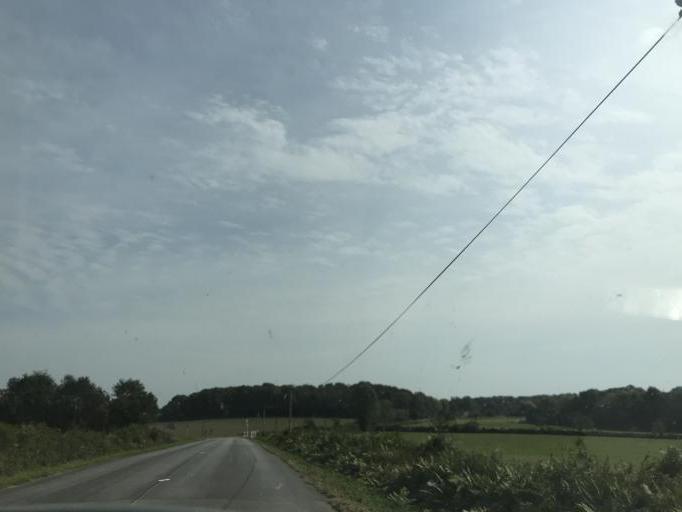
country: FR
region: Brittany
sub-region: Departement du Finistere
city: Loperec
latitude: 48.2958
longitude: -4.0153
